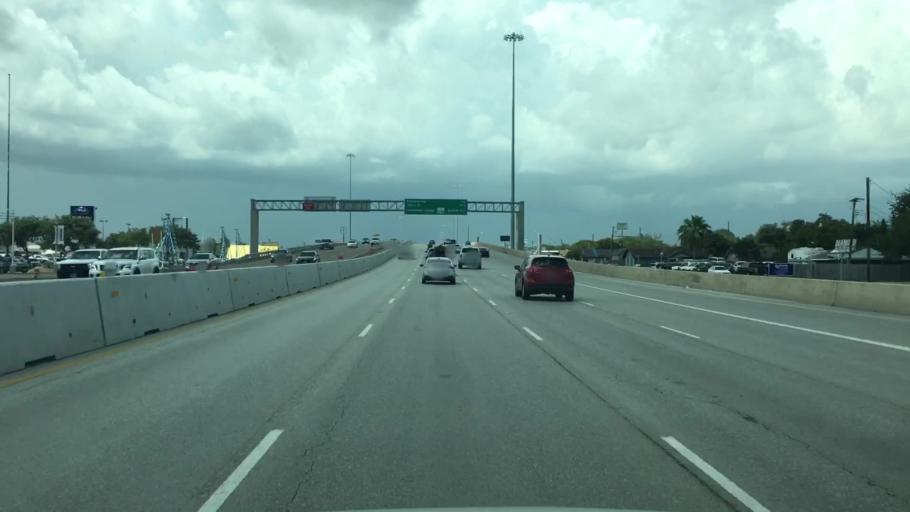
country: US
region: Texas
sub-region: Nueces County
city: Corpus Christi
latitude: 27.7237
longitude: -97.4028
